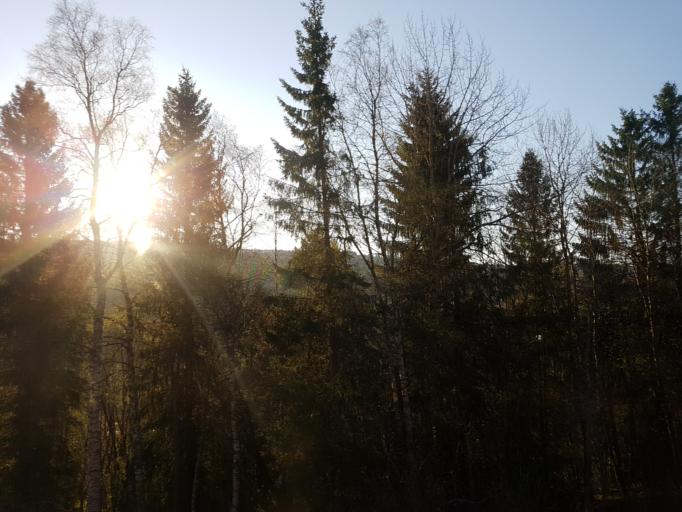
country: NO
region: Sor-Trondelag
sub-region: Midtre Gauldal
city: Storen
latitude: 62.9434
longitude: 10.1835
